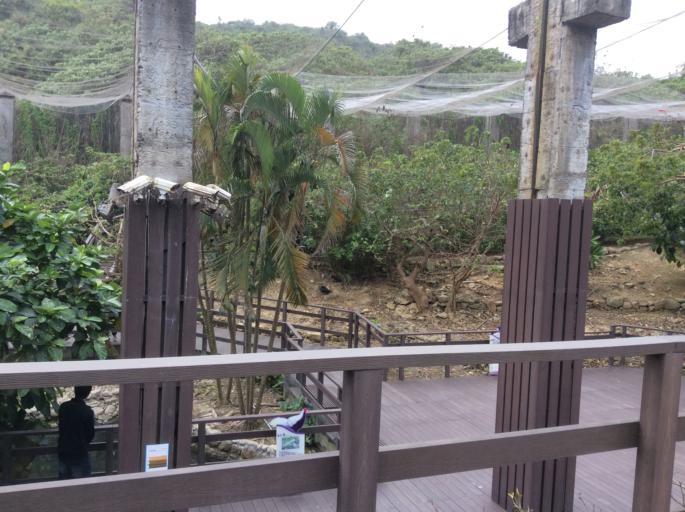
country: TW
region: Kaohsiung
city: Kaohsiung
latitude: 22.6375
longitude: 120.2752
